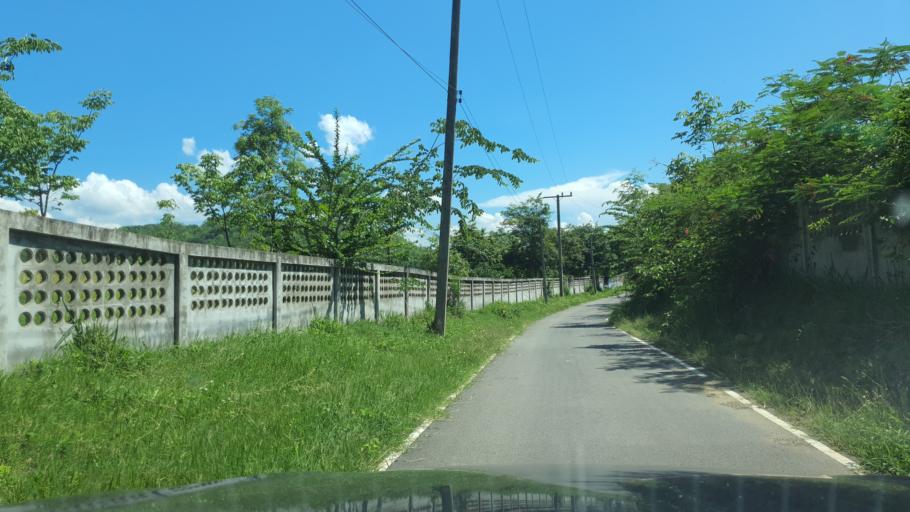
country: TH
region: Chiang Mai
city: Mae On
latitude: 18.8021
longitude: 99.2685
